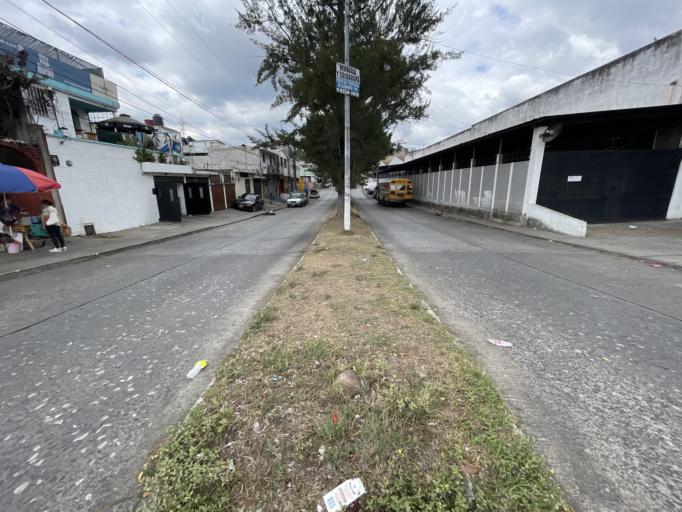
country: GT
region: Guatemala
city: Mixco
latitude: 14.6615
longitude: -90.5854
